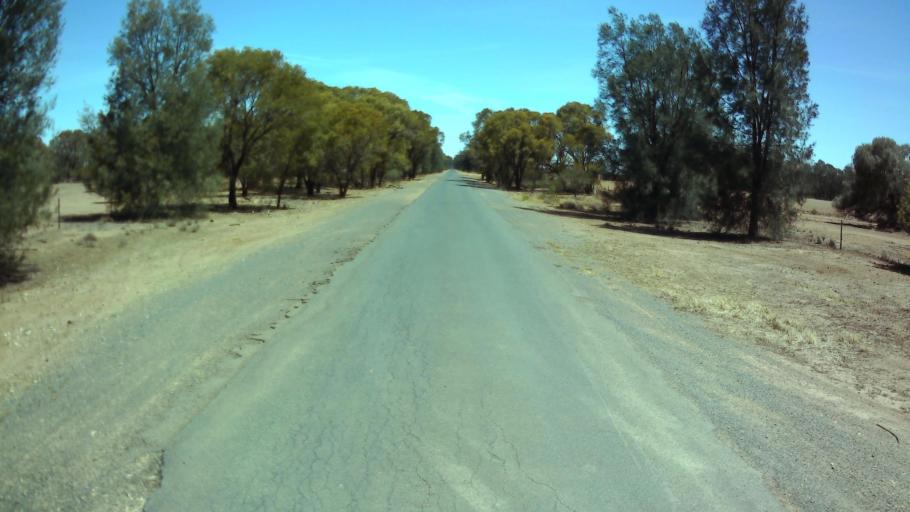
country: AU
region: New South Wales
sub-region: Weddin
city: Grenfell
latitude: -33.8709
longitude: 147.6919
